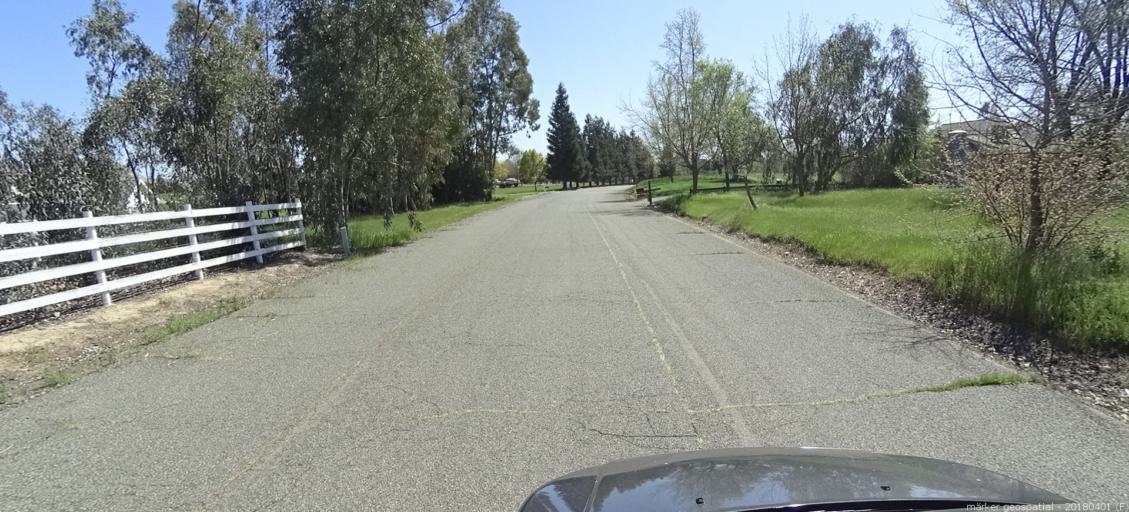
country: US
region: California
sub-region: Sacramento County
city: Wilton
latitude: 38.4164
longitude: -121.2183
